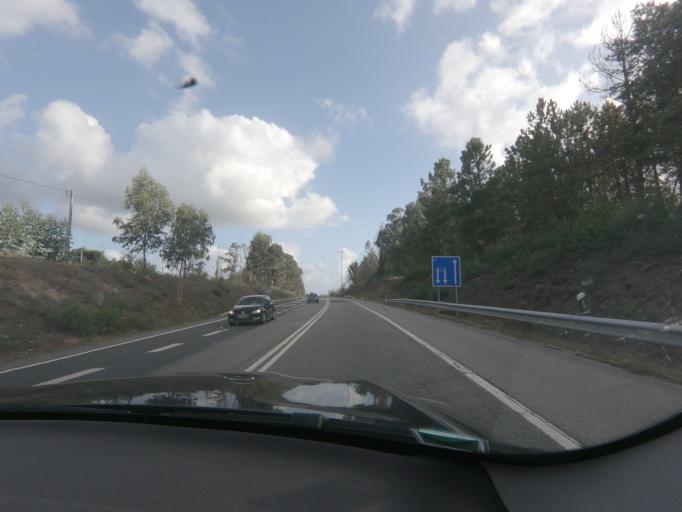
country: PT
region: Viseu
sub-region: Concelho de Tondela
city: Tondela
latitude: 40.5639
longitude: -8.0506
